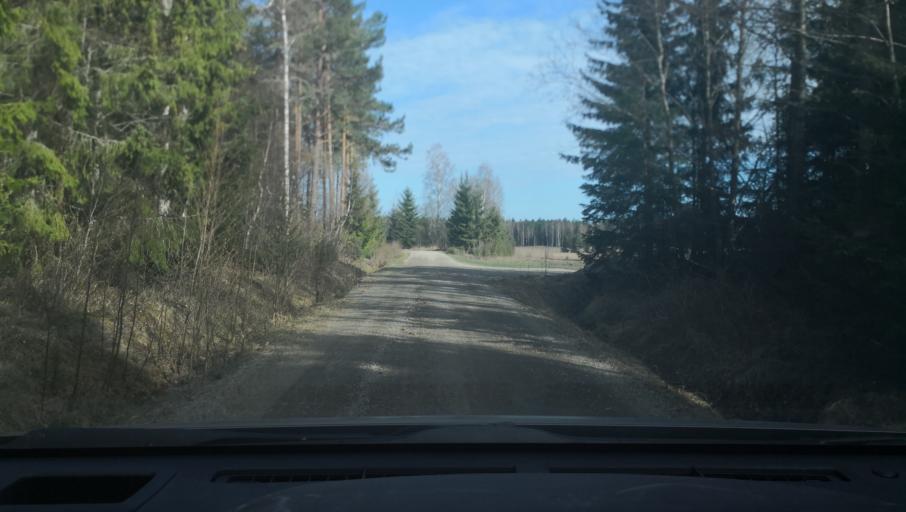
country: SE
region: Uppsala
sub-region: Heby Kommun
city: Heby
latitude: 59.8391
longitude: 16.8741
